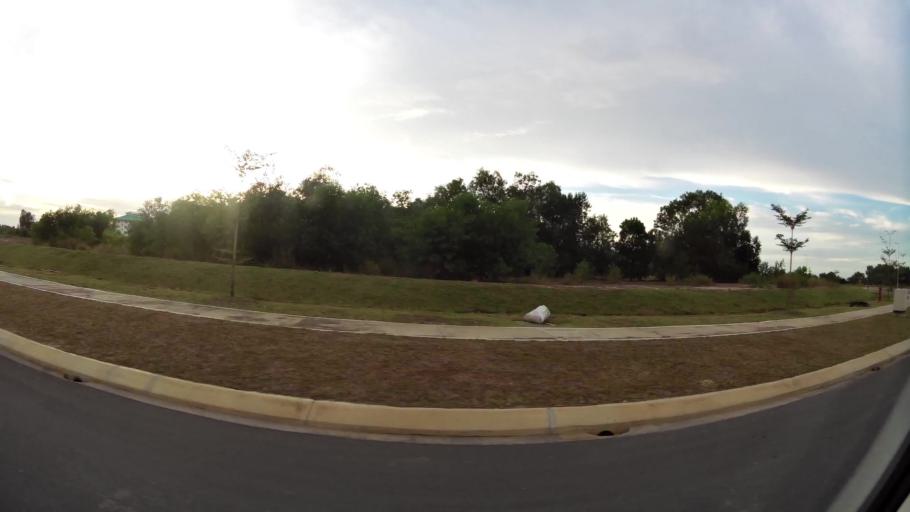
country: BN
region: Brunei and Muara
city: Bandar Seri Begawan
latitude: 4.9923
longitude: 114.9853
